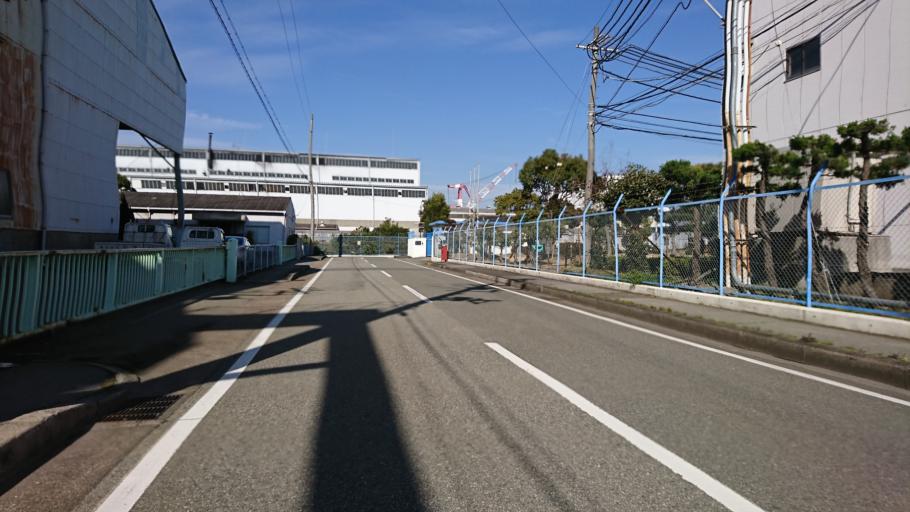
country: JP
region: Hyogo
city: Kakogawacho-honmachi
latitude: 34.6961
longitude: 134.8536
